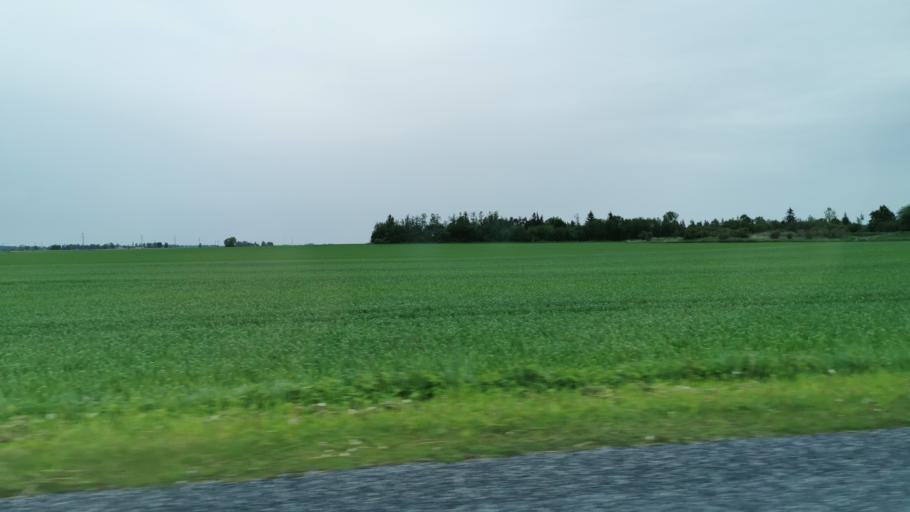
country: EE
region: Laeaene-Virumaa
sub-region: Vaeike-Maarja vald
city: Vaike-Maarja
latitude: 59.1610
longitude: 26.2755
